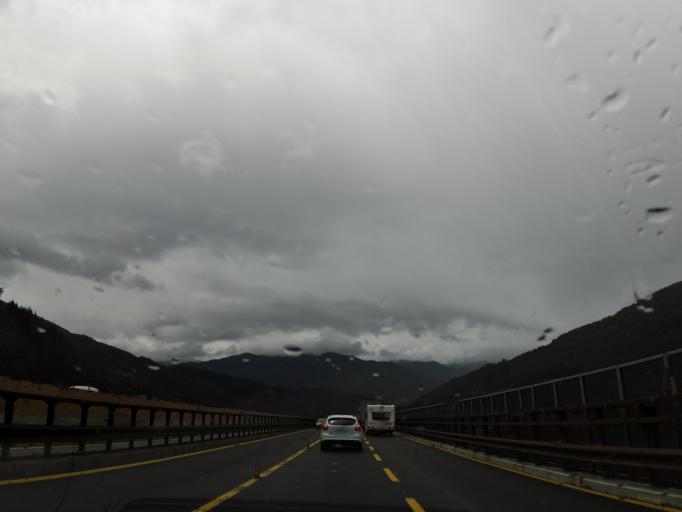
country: IT
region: Trentino-Alto Adige
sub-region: Bolzano
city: Brennero - Brenner
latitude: 46.9377
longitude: 11.4490
